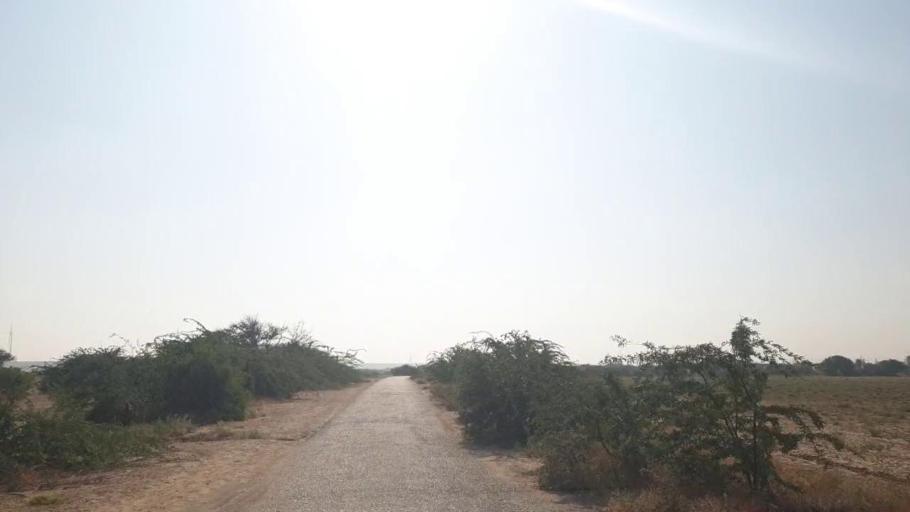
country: PK
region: Sindh
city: Thatta
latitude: 25.1315
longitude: 67.7751
